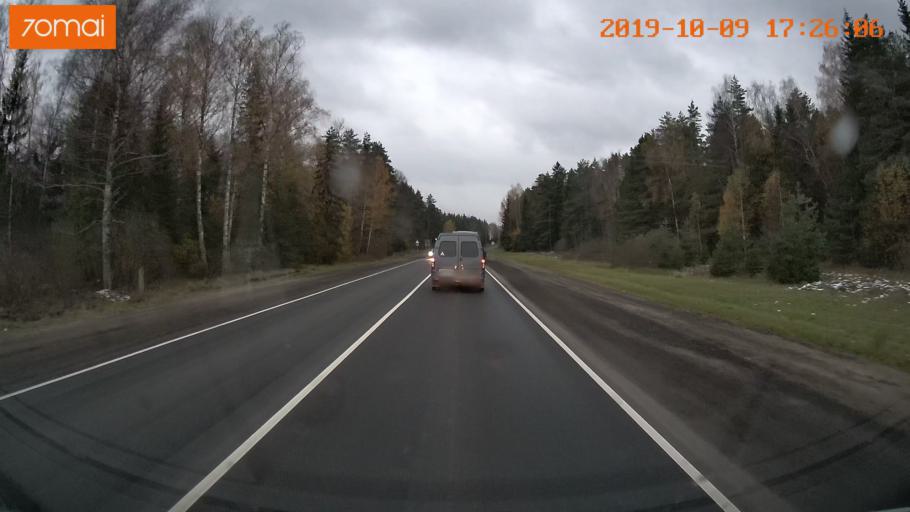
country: RU
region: Ivanovo
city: Furmanov
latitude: 57.1765
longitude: 41.0823
